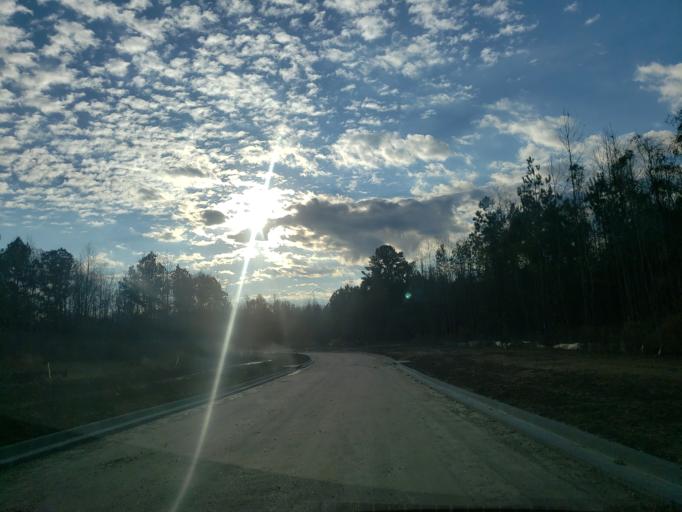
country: US
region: Georgia
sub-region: Chatham County
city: Pooler
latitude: 32.1279
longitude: -81.2458
